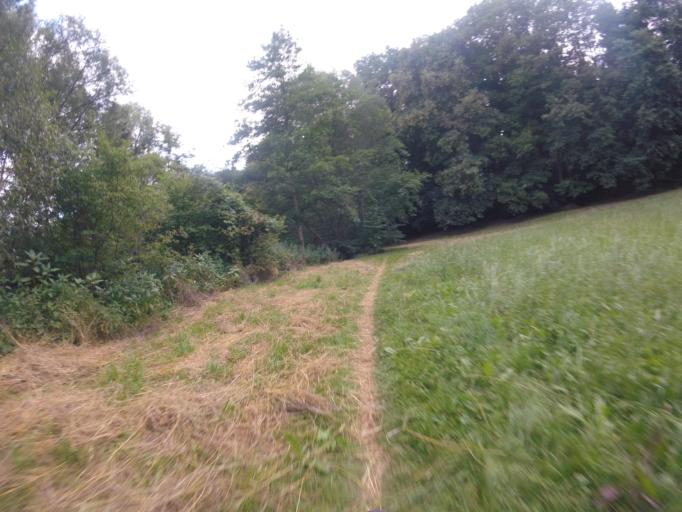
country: DE
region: Baden-Wuerttemberg
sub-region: Regierungsbezirk Stuttgart
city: Oppenweiler
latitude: 48.9623
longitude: 9.4623
